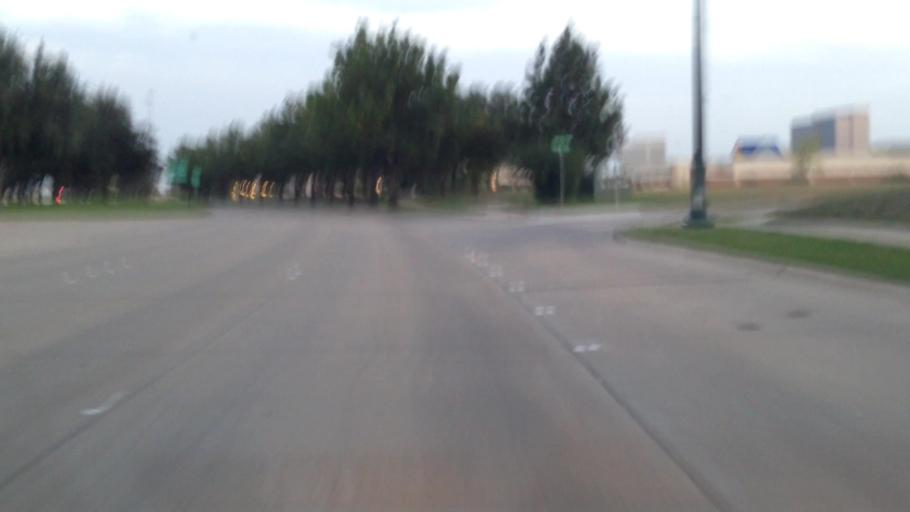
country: US
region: Texas
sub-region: Collin County
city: Frisco
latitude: 33.0971
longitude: -96.8172
